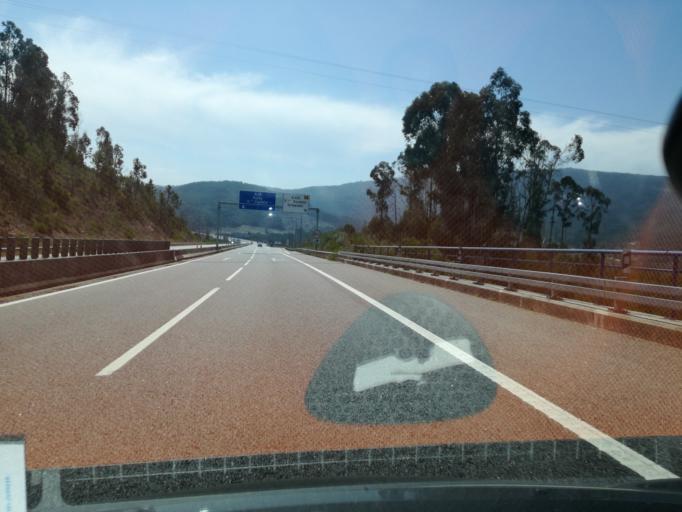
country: PT
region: Viana do Castelo
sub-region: Caminha
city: Vila Praia de Ancora
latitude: 41.8098
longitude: -8.8049
